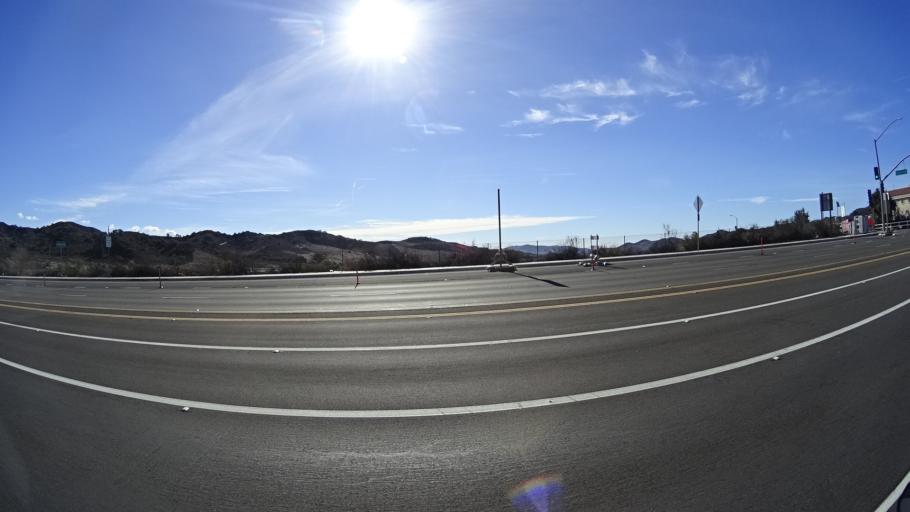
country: US
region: California
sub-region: Orange County
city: Las Flores
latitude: 33.5862
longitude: -117.6127
